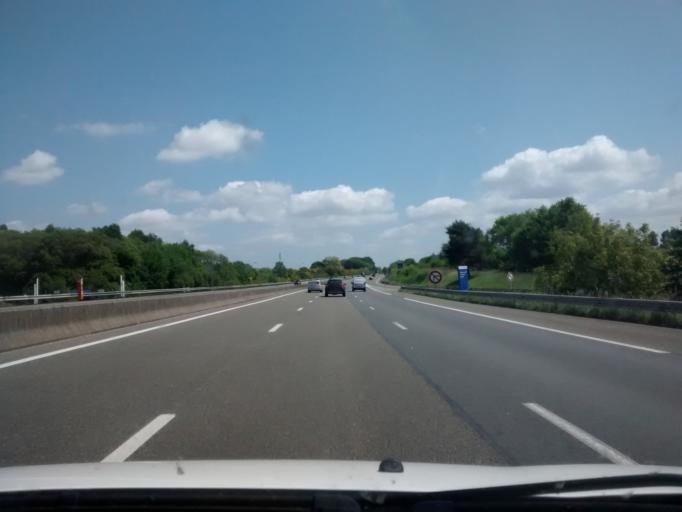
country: FR
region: Pays de la Loire
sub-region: Departement de la Sarthe
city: Sarge-les-le-Mans
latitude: 48.0555
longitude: 0.2542
